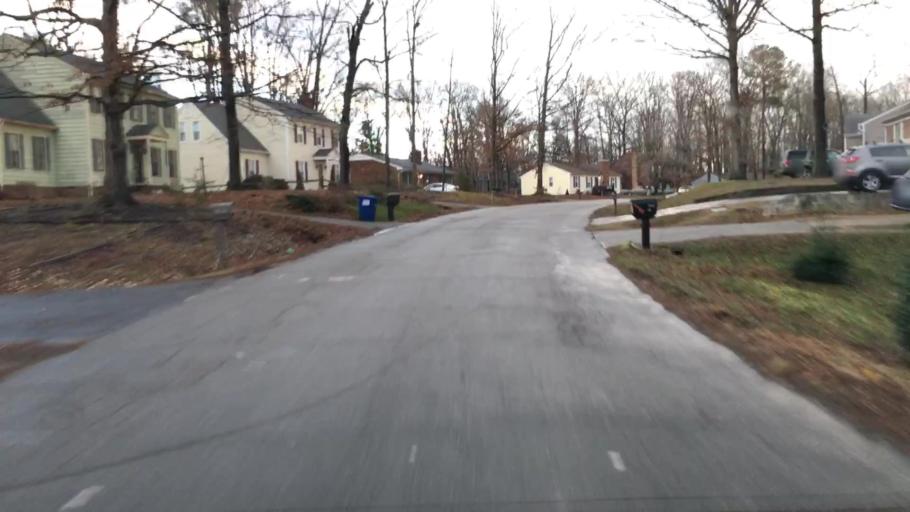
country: US
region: Virginia
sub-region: Chesterfield County
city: Bon Air
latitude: 37.5173
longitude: -77.6193
